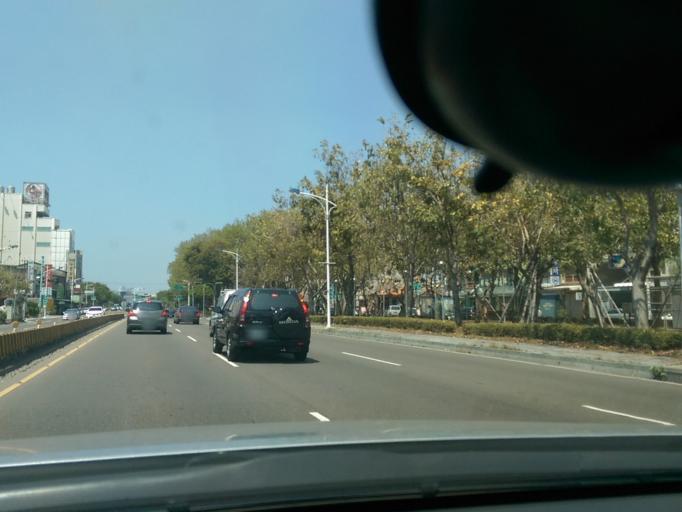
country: TW
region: Taiwan
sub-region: Chiayi
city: Jiayi Shi
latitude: 23.4881
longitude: 120.4532
